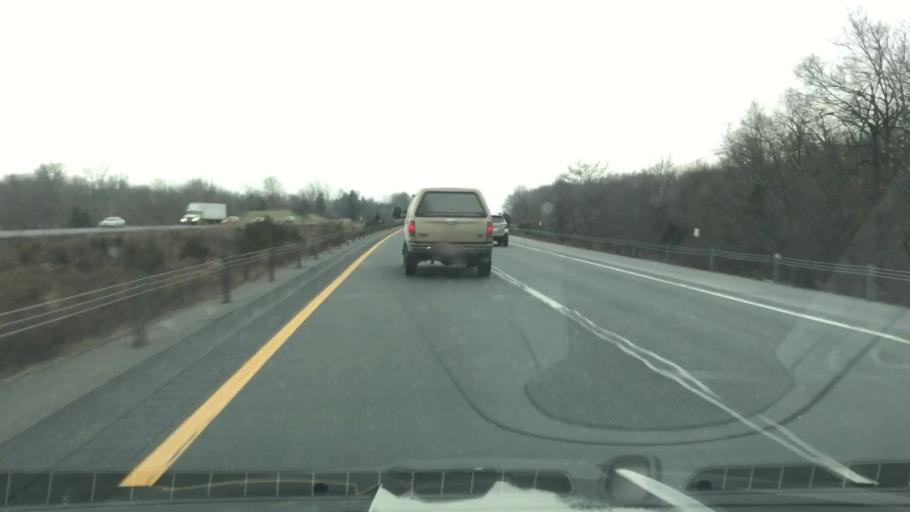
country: US
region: New York
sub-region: Orange County
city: Orange Lake
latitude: 41.5128
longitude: -74.1510
